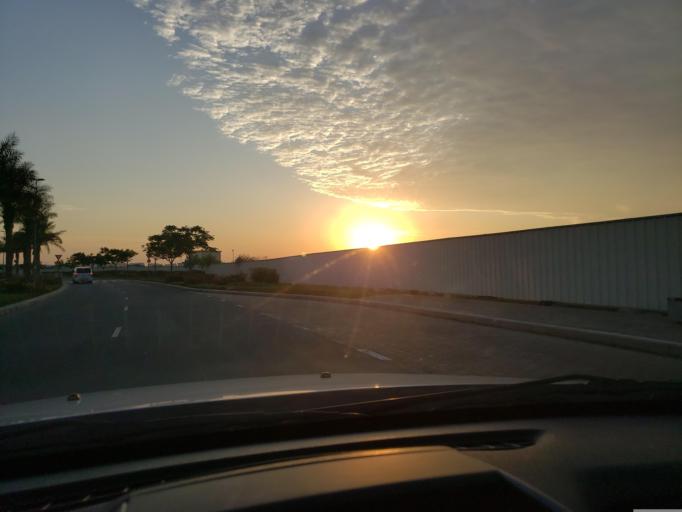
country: AE
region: Dubai
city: Dubai
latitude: 25.0187
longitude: 55.2684
